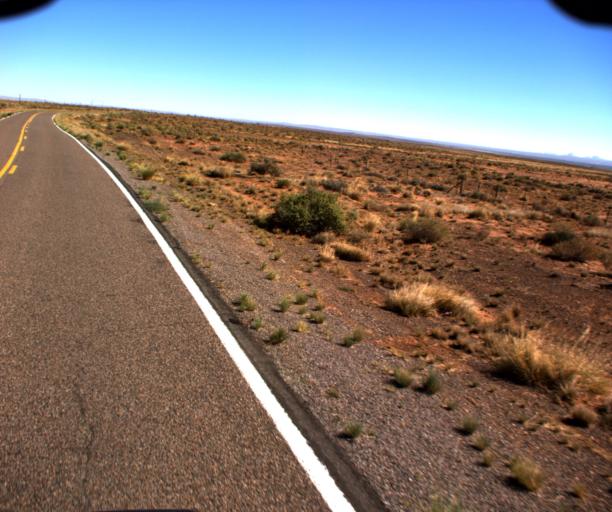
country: US
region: Arizona
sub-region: Coconino County
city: LeChee
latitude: 35.0913
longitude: -110.8605
